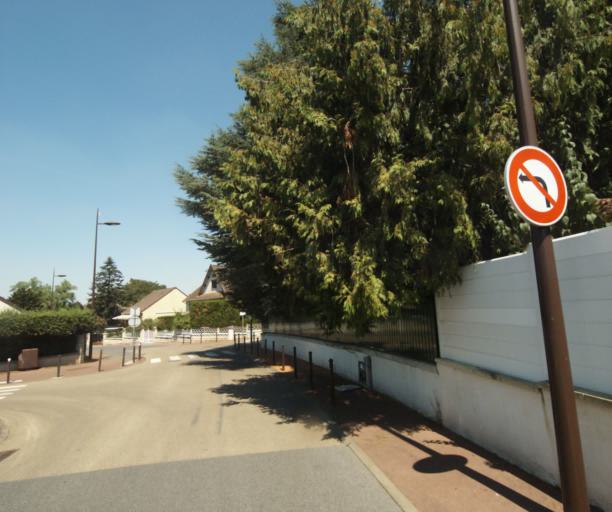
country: FR
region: Ile-de-France
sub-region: Departement de Seine-et-Marne
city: Lagny-sur-Marne
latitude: 48.8755
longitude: 2.7292
